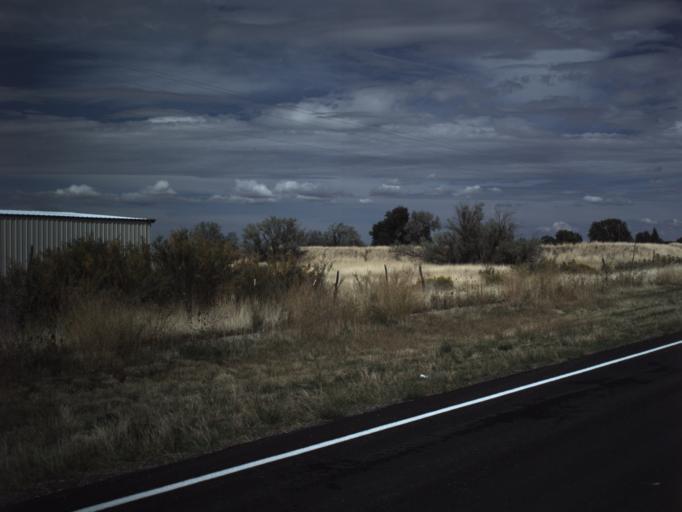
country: US
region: Utah
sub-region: Millard County
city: Fillmore
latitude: 38.8777
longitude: -112.4125
